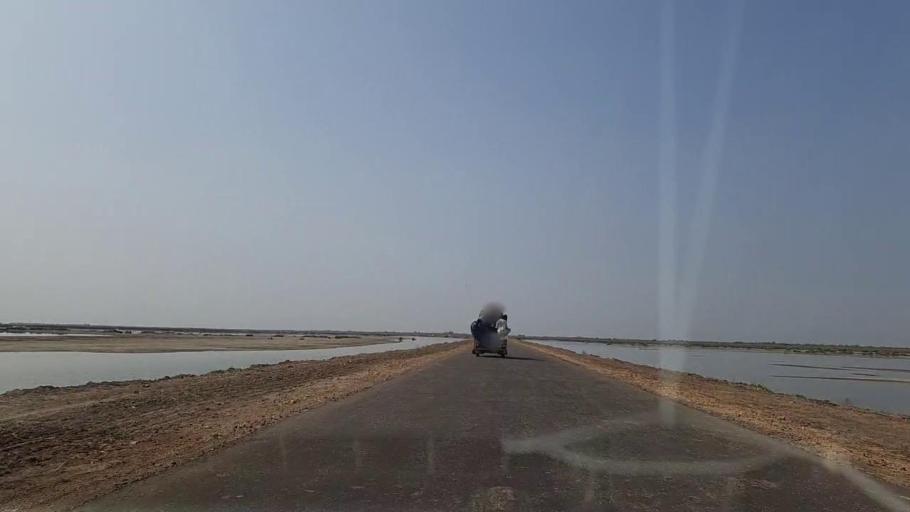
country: PK
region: Sindh
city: Chuhar Jamali
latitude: 24.2234
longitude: 67.8870
